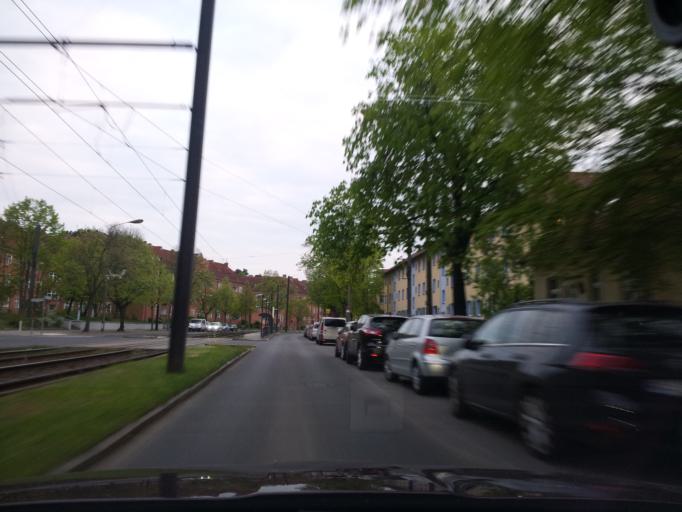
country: DE
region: Berlin
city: Kopenick Bezirk
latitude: 52.4647
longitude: 13.5840
